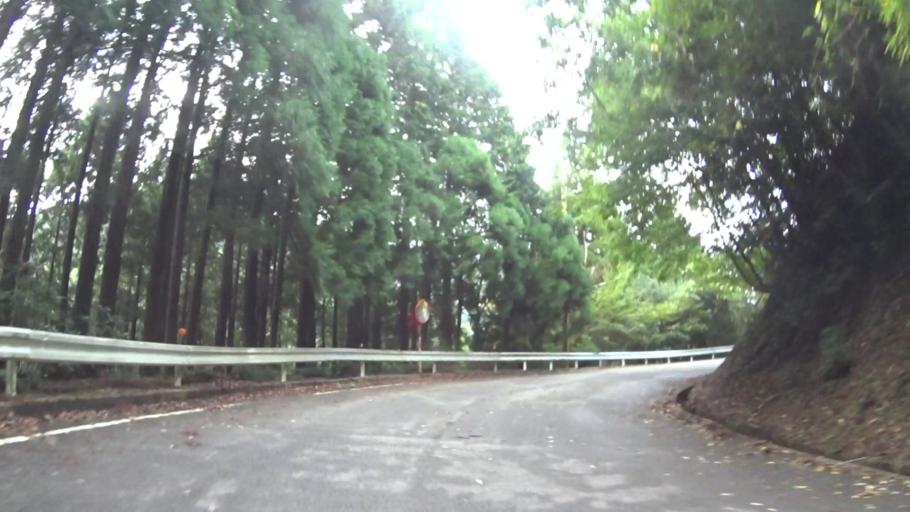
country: JP
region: Shiga Prefecture
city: Kitahama
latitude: 35.2705
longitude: 135.7384
